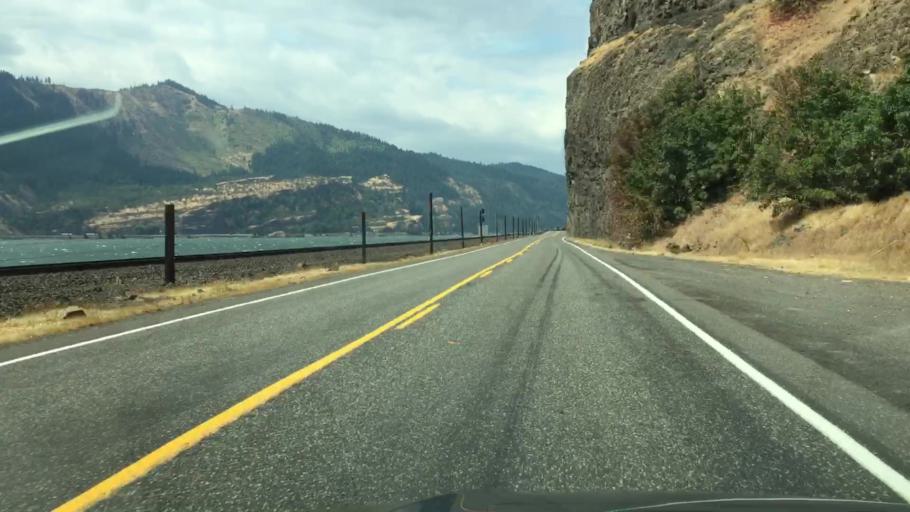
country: US
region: Washington
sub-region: Klickitat County
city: White Salmon
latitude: 45.6994
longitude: -121.4176
